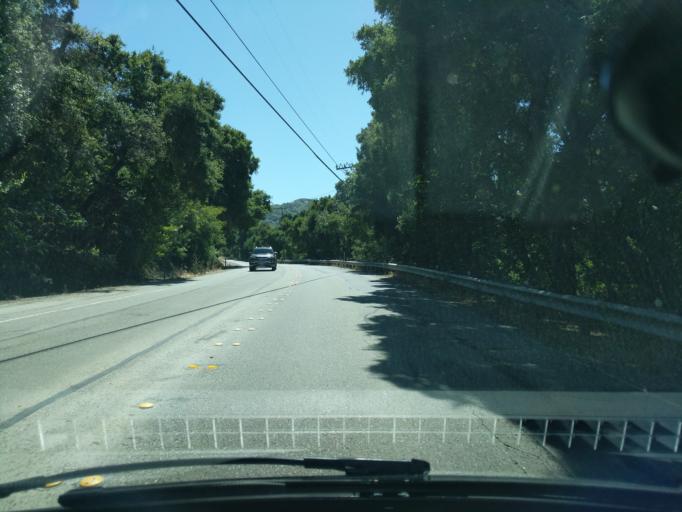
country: US
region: California
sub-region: Contra Costa County
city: San Ramon
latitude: 37.7621
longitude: -122.0249
